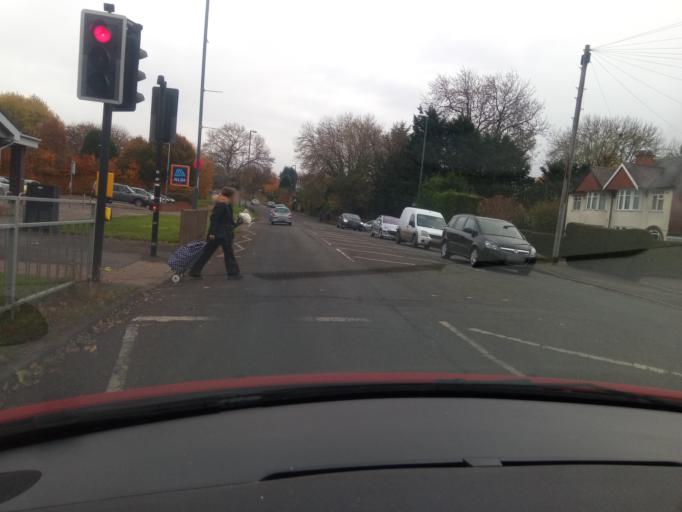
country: GB
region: England
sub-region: Derby
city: Derby
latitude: 52.9237
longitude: -1.4372
